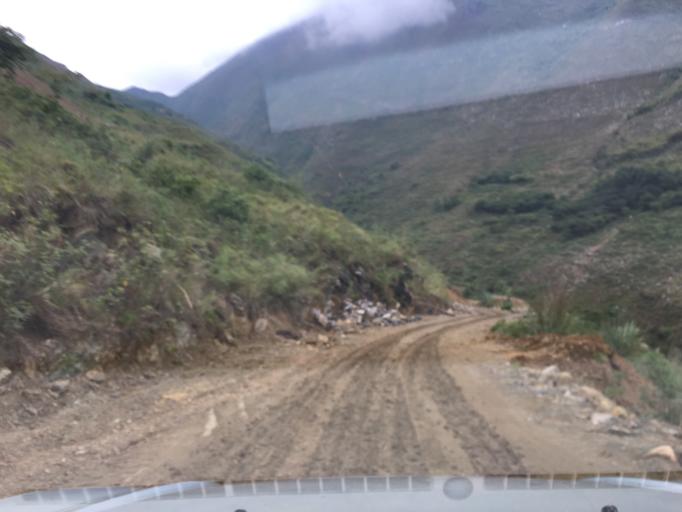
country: CN
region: Guizhou Sheng
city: Anshun
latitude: 25.9633
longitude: 105.2397
